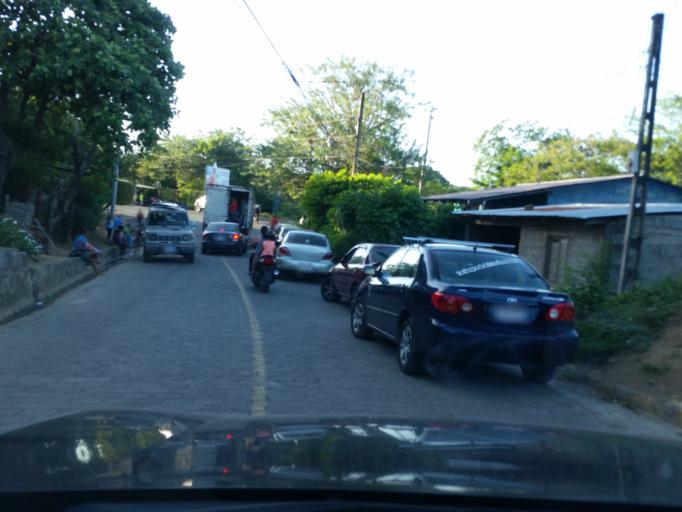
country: NI
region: Rivas
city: San Juan del Sur
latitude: 11.2570
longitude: -85.8644
